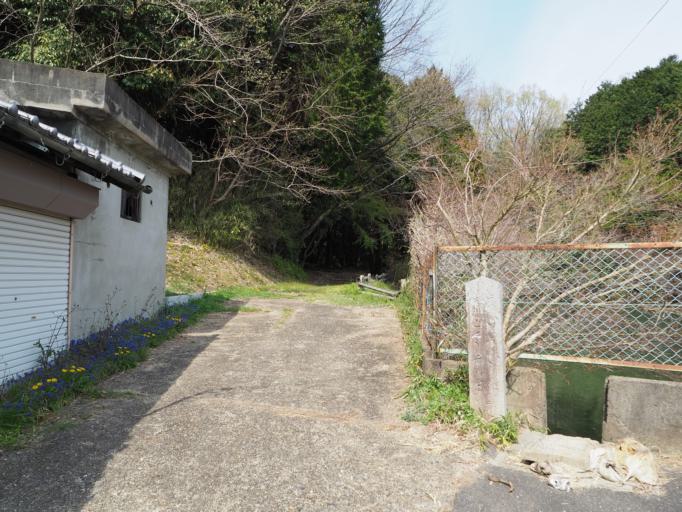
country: JP
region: Nara
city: Tenri
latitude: 34.6275
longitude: 135.8528
